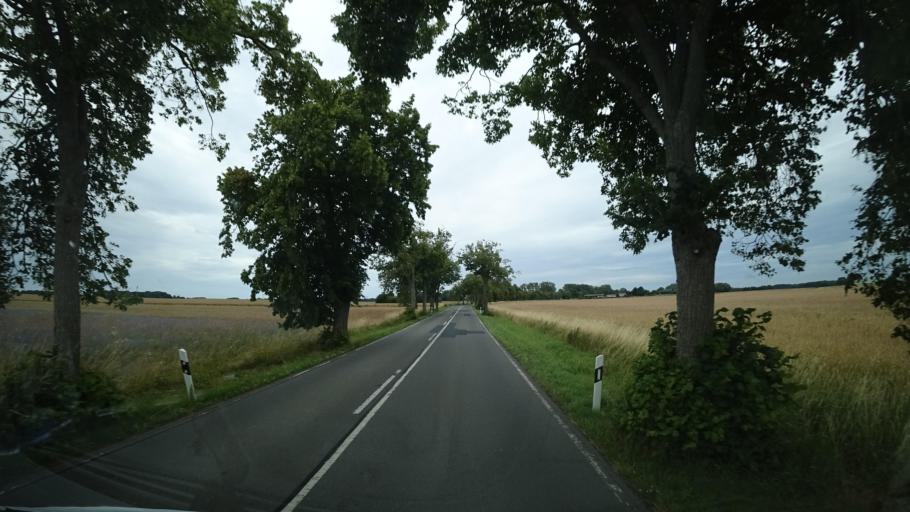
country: DE
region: Mecklenburg-Vorpommern
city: Poseritz
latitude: 54.3011
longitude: 13.3046
